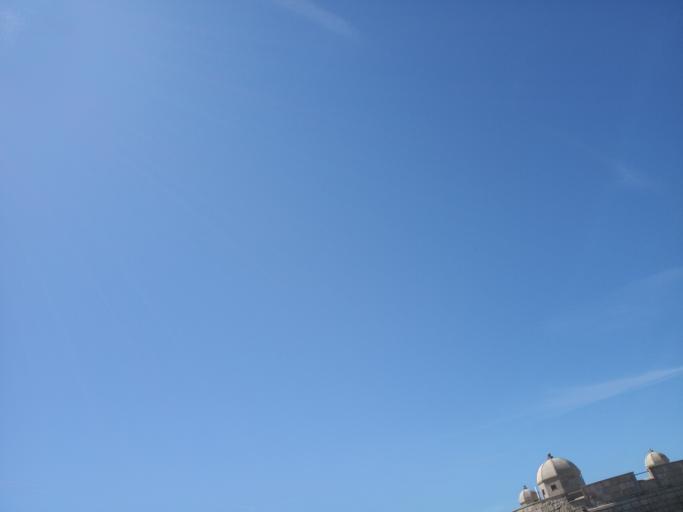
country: ES
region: Galicia
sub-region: Provincia de Pontevedra
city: A Guarda
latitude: 41.9030
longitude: -8.8799
